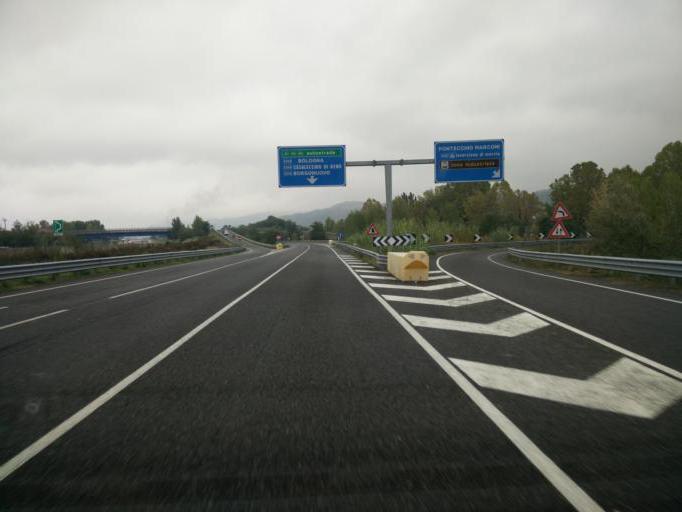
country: IT
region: Emilia-Romagna
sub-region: Provincia di Bologna
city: Borgonuovo
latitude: 44.4281
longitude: 11.2755
